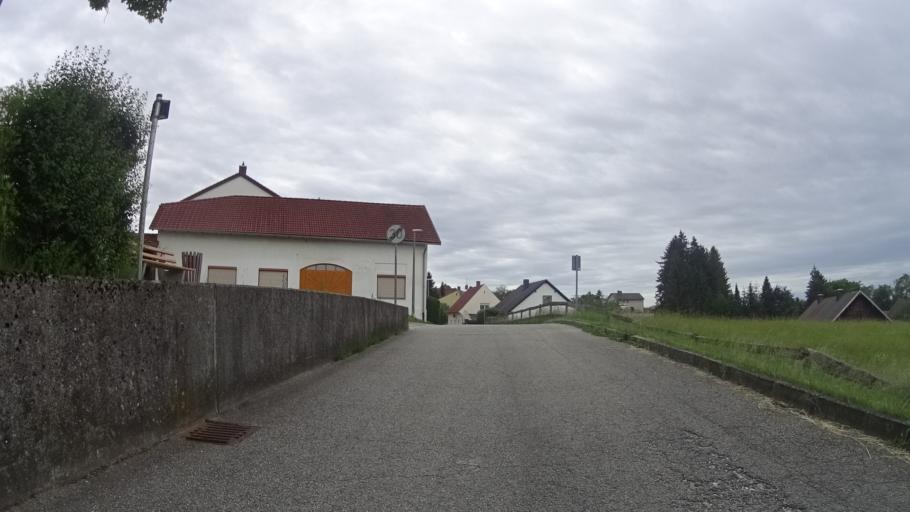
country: DE
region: Bavaria
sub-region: Lower Bavaria
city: Velden
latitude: 48.3687
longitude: 12.2559
